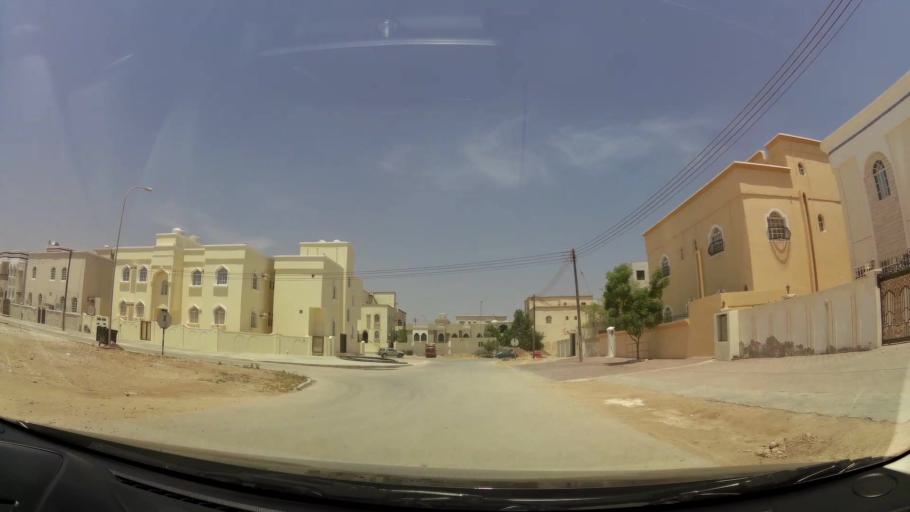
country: OM
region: Zufar
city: Salalah
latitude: 17.0747
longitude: 54.1494
